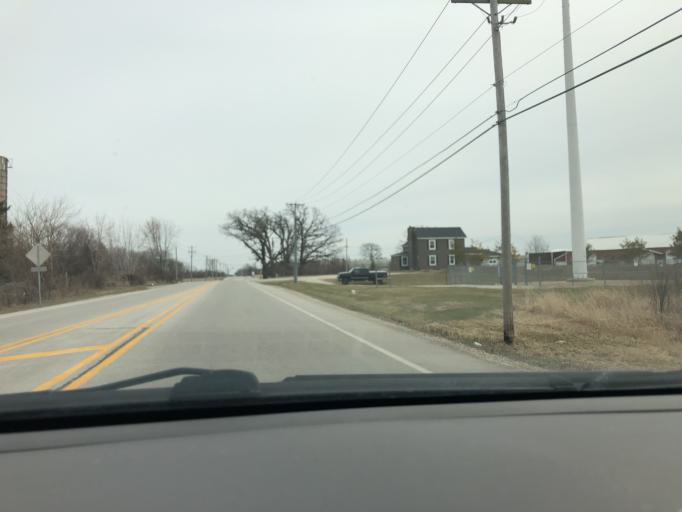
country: US
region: Illinois
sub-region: Kane County
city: Gilberts
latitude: 42.0702
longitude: -88.3464
